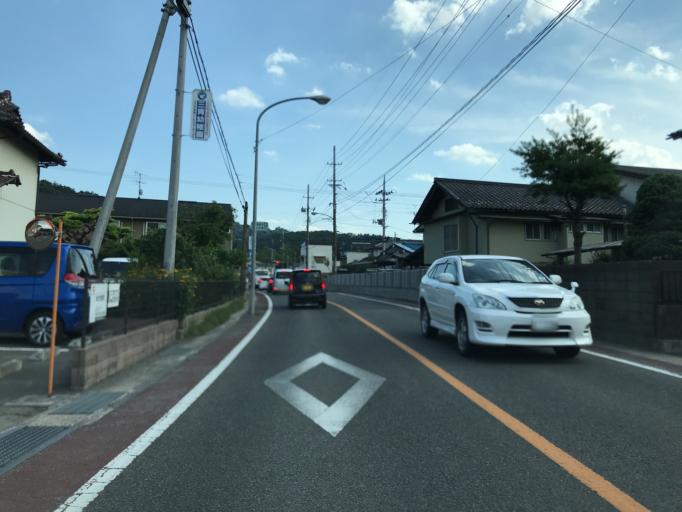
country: JP
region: Fukushima
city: Fukushima-shi
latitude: 37.7724
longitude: 140.4966
